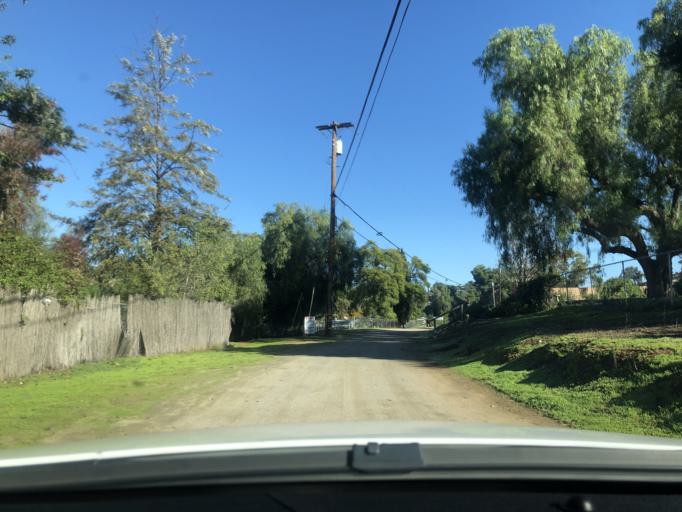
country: US
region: California
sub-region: San Diego County
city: Rancho San Diego
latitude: 32.7728
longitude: -116.9381
